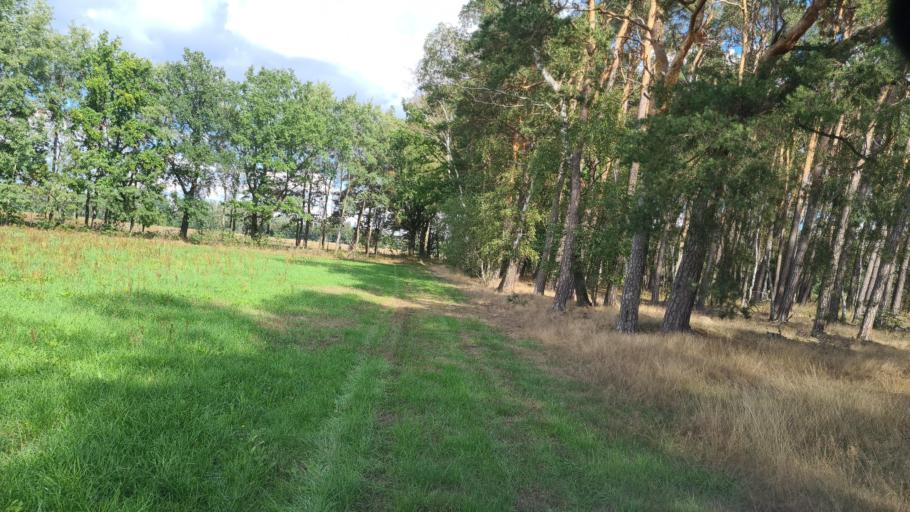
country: DE
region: Brandenburg
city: Finsterwalde
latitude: 51.6575
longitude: 13.7490
